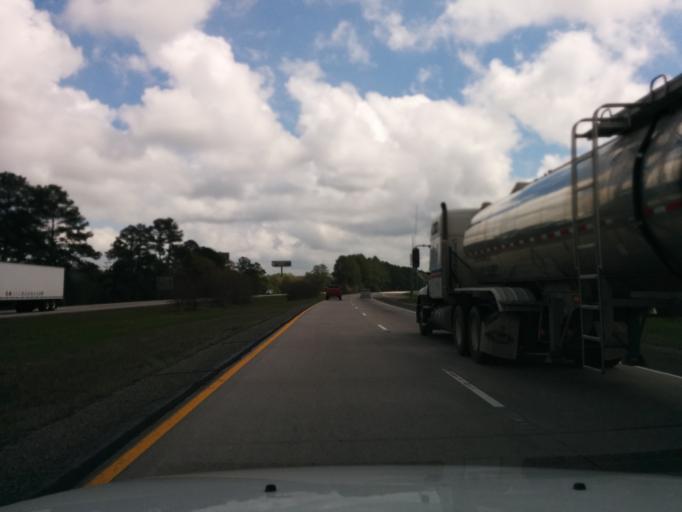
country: US
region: Georgia
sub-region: Bulloch County
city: Brooklet
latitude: 32.2554
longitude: -81.7084
